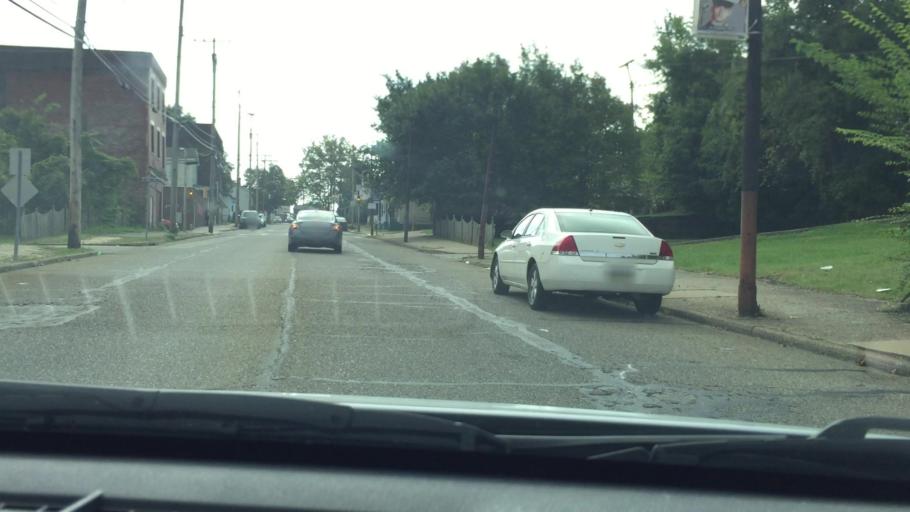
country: US
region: Pennsylvania
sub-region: Allegheny County
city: Homestead
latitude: 40.4036
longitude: -79.9090
